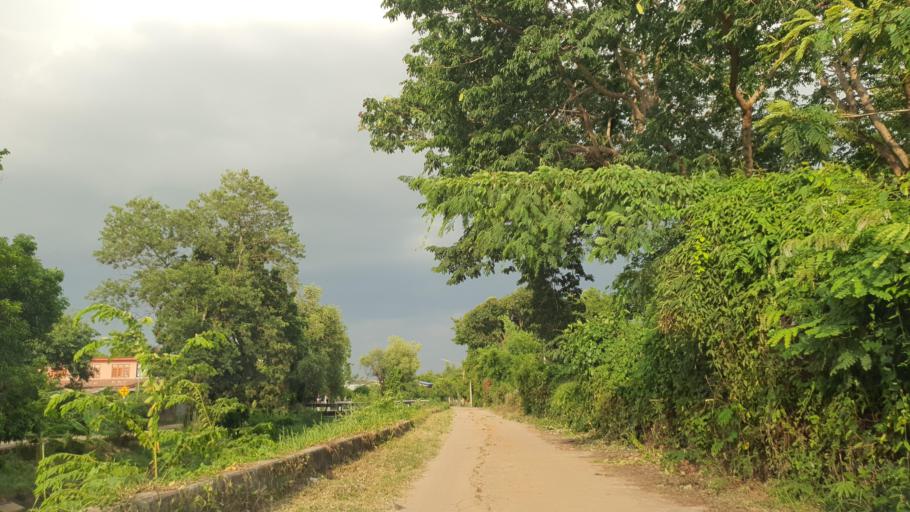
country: TH
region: Sukhothai
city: Ban Na
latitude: 17.0135
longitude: 99.7754
